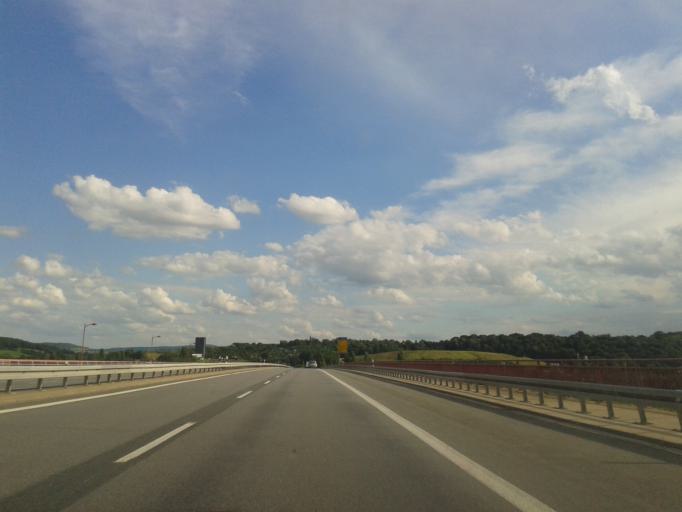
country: DE
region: Saxony
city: Pirna
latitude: 50.9635
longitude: 13.9160
